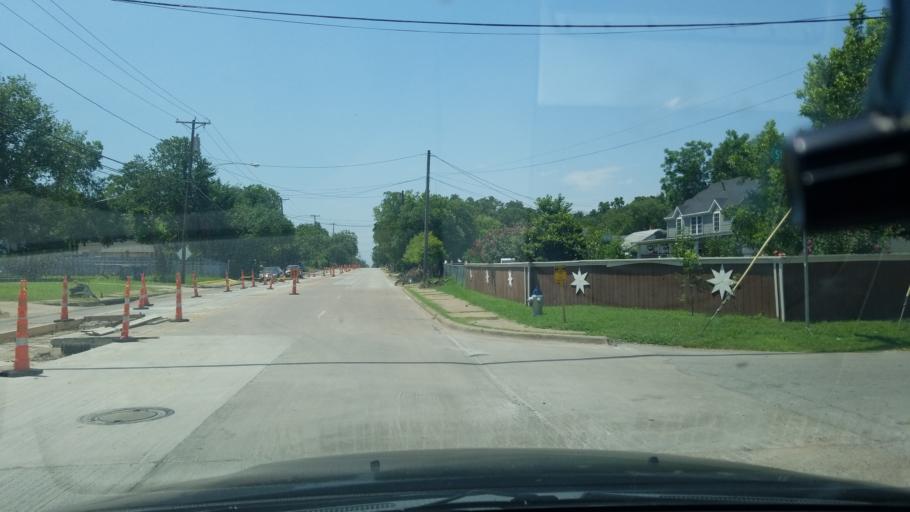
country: US
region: Texas
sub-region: Dallas County
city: Balch Springs
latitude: 32.7416
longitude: -96.6787
